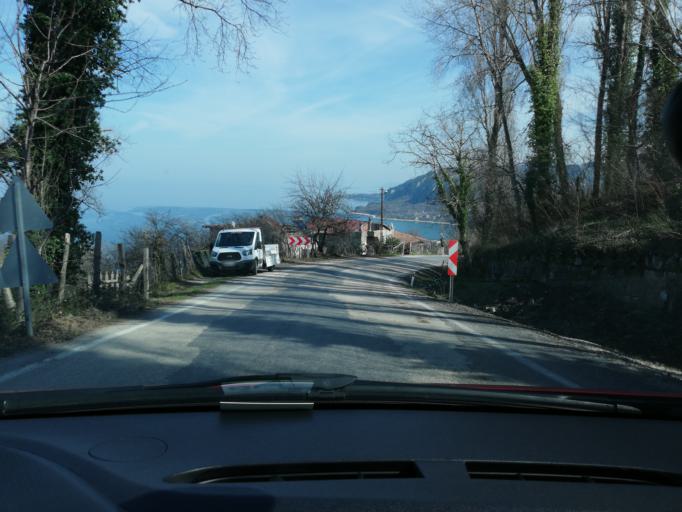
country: TR
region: Bartin
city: Kurucasile
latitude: 41.8279
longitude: 32.6565
